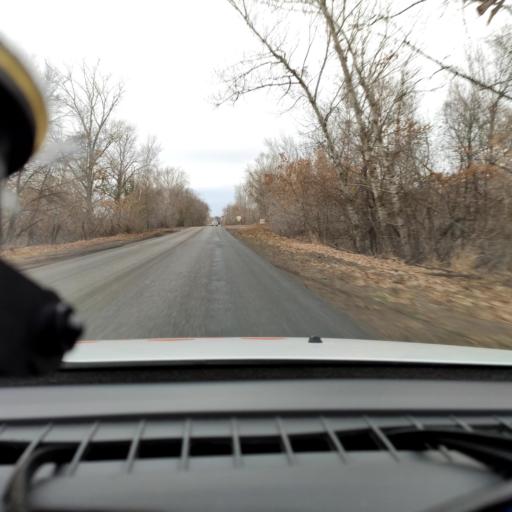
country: RU
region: Samara
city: Samara
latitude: 53.1241
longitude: 50.2345
